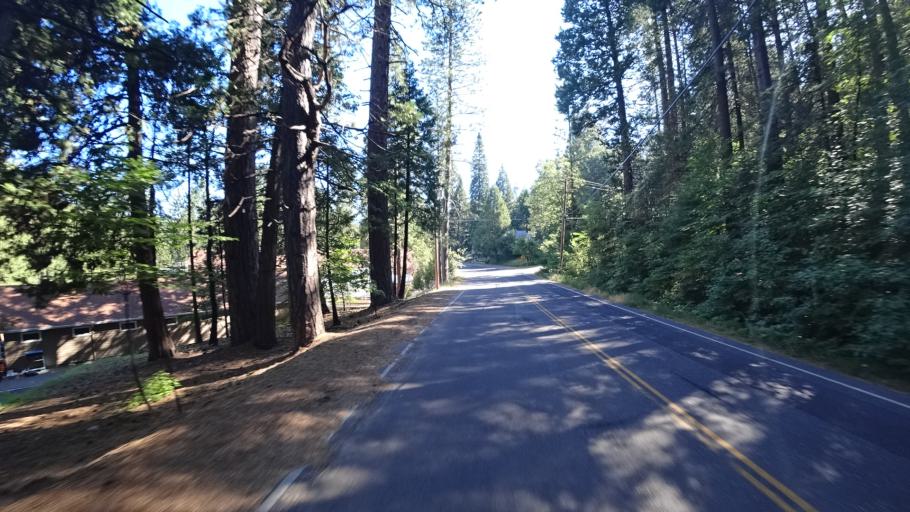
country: US
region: California
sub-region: Calaveras County
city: Arnold
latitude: 38.2621
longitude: -120.3423
